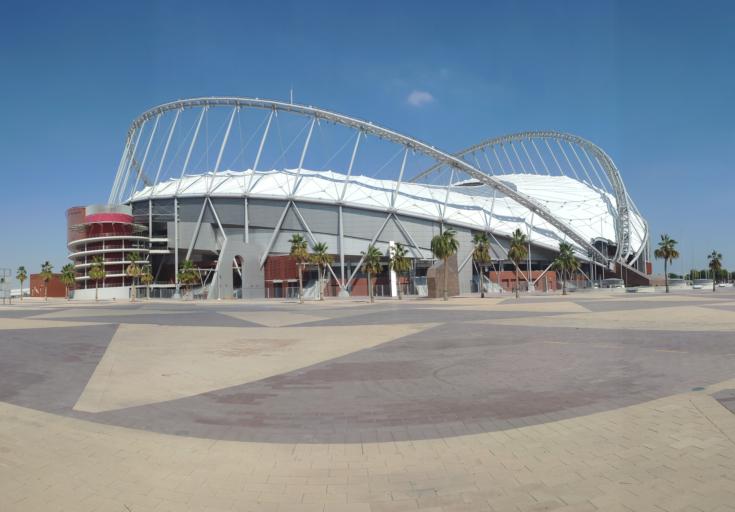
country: QA
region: Baladiyat ar Rayyan
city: Ar Rayyan
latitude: 25.2618
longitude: 51.4470
